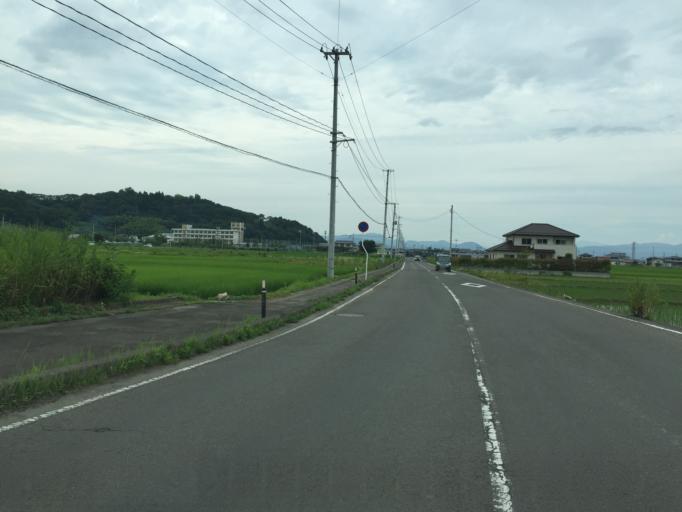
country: JP
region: Fukushima
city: Fukushima-shi
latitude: 37.7190
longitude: 140.4394
